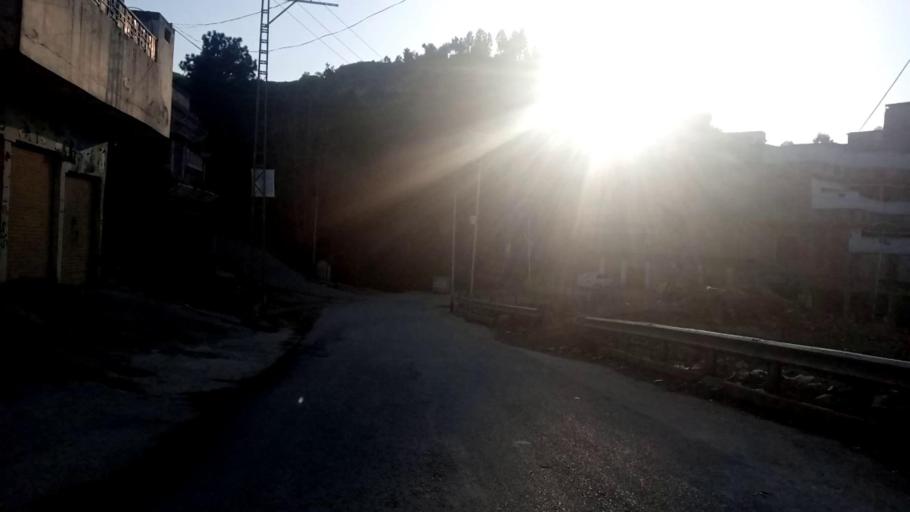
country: PK
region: Khyber Pakhtunkhwa
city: Saidu Sharif
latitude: 34.7432
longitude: 72.3518
